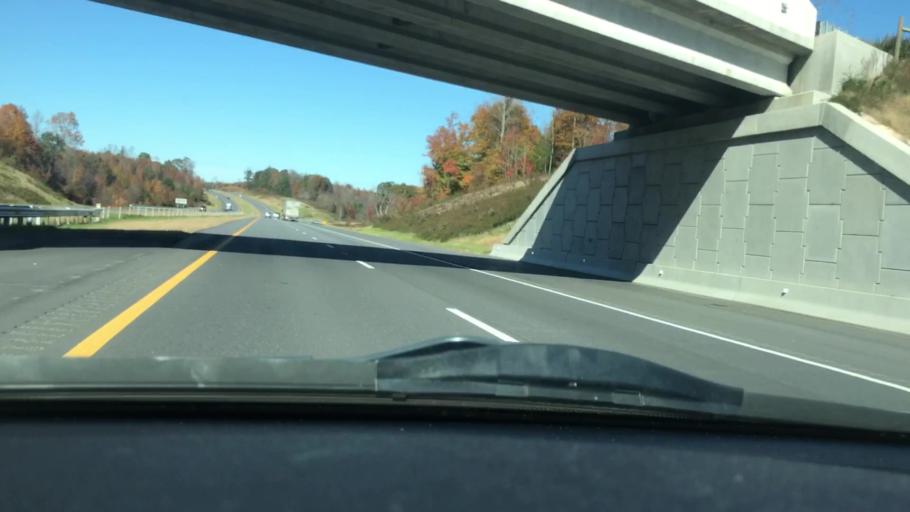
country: US
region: North Carolina
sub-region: Guilford County
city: Summerfield
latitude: 36.1841
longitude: -79.9314
